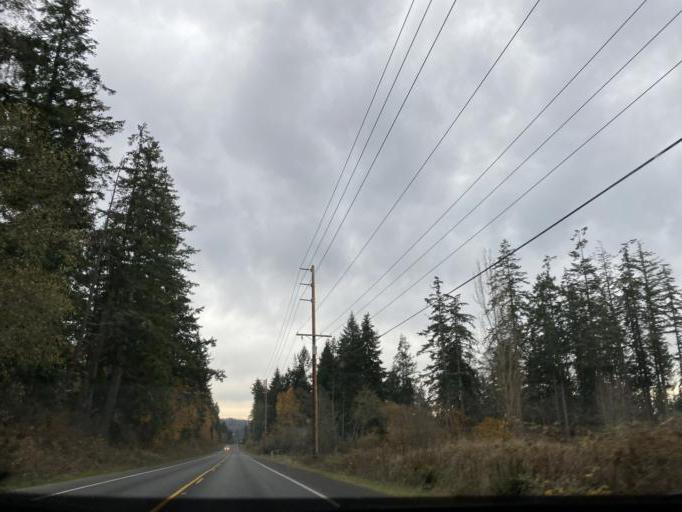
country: US
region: Washington
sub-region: Island County
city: Freeland
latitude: 48.0145
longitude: -122.5574
